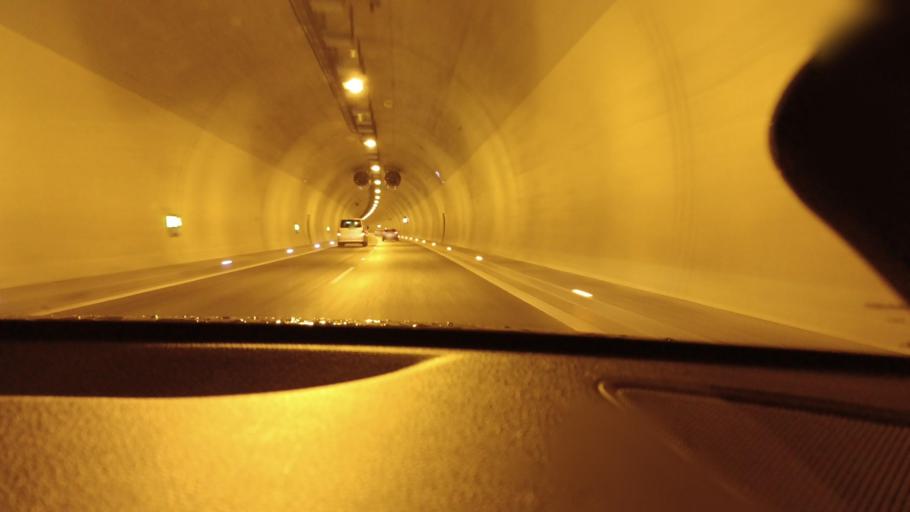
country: SK
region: Presovsky
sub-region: Okres Presov
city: Presov
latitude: 48.9675
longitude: 21.2404
